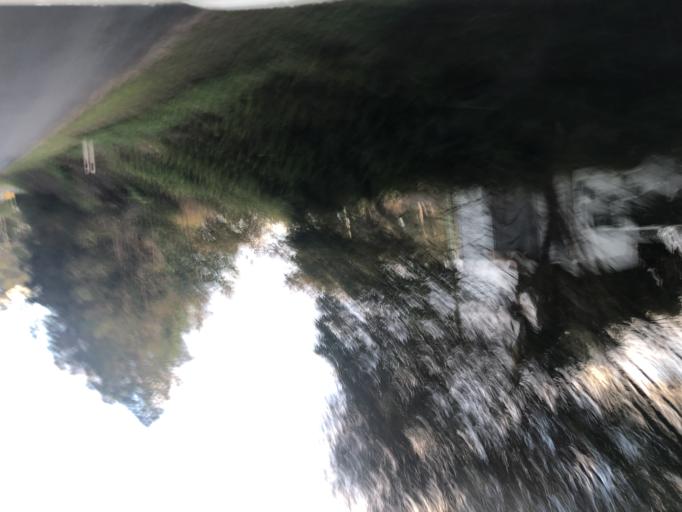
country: AU
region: New South Wales
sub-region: Nambucca Shire
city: Macksville
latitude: -30.7292
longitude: 152.9154
